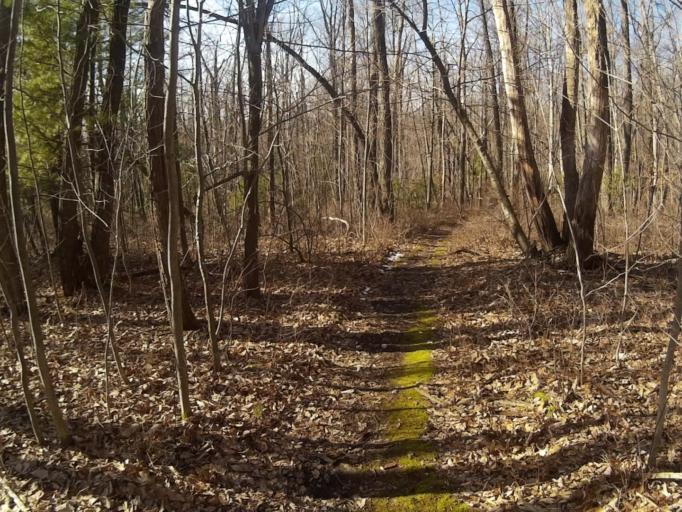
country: US
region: Pennsylvania
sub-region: Centre County
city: Lemont
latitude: 40.8110
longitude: -77.7831
